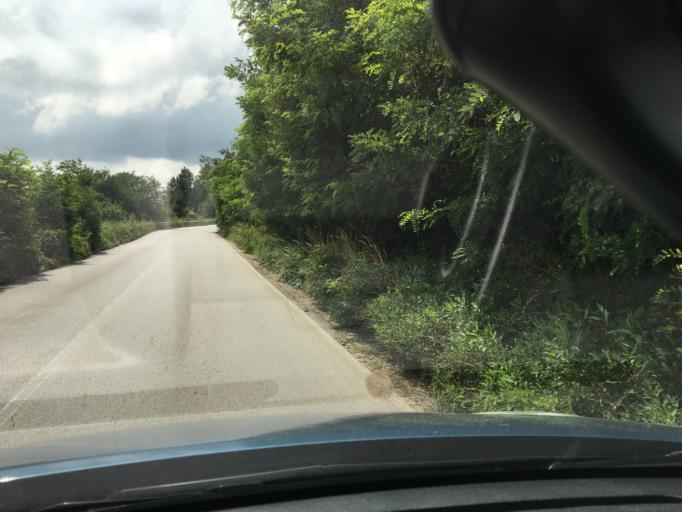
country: BG
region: Sofia-Capital
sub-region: Stolichna Obshtina
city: Sofia
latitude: 42.6025
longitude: 23.3685
